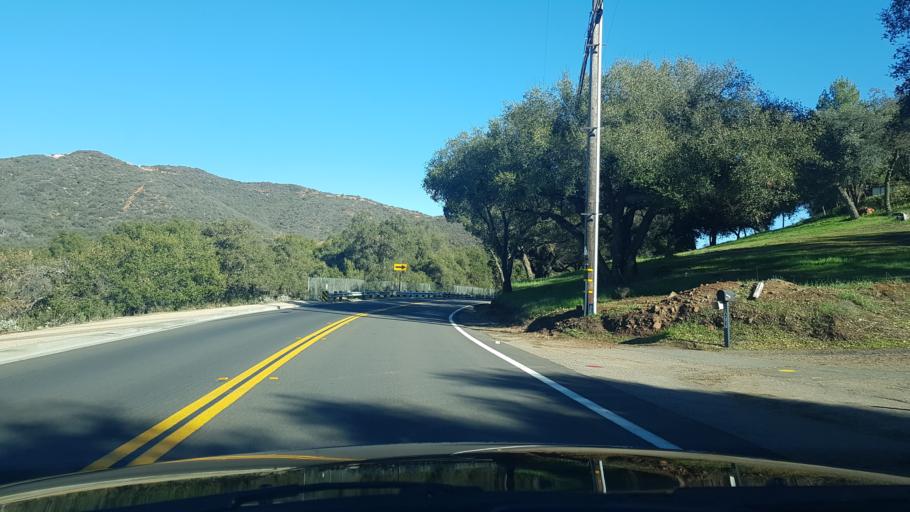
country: US
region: California
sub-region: San Diego County
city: Valley Center
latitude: 33.2053
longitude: -117.0109
